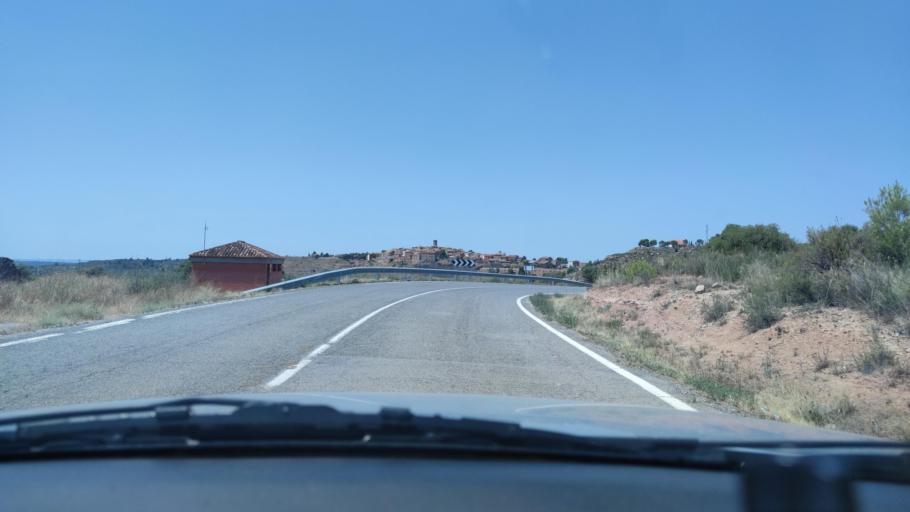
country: ES
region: Catalonia
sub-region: Provincia de Lleida
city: el Cogul
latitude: 41.4293
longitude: 0.6594
